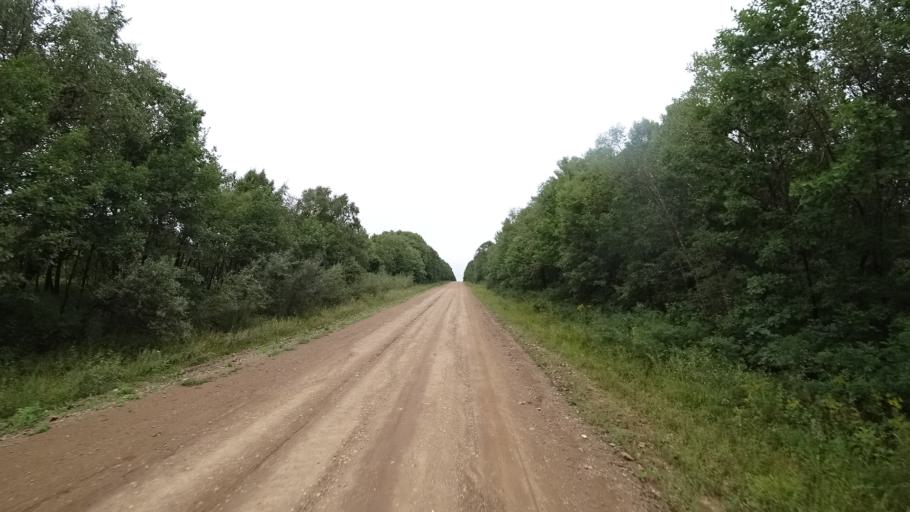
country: RU
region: Primorskiy
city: Ivanovka
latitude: 44.0279
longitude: 132.5271
